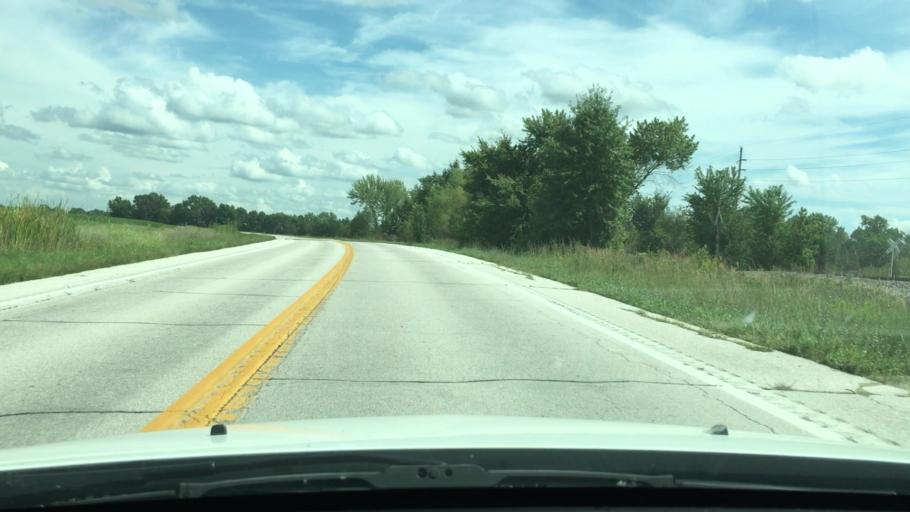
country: US
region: Missouri
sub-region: Audrain County
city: Vandalia
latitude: 39.3371
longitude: -91.4229
